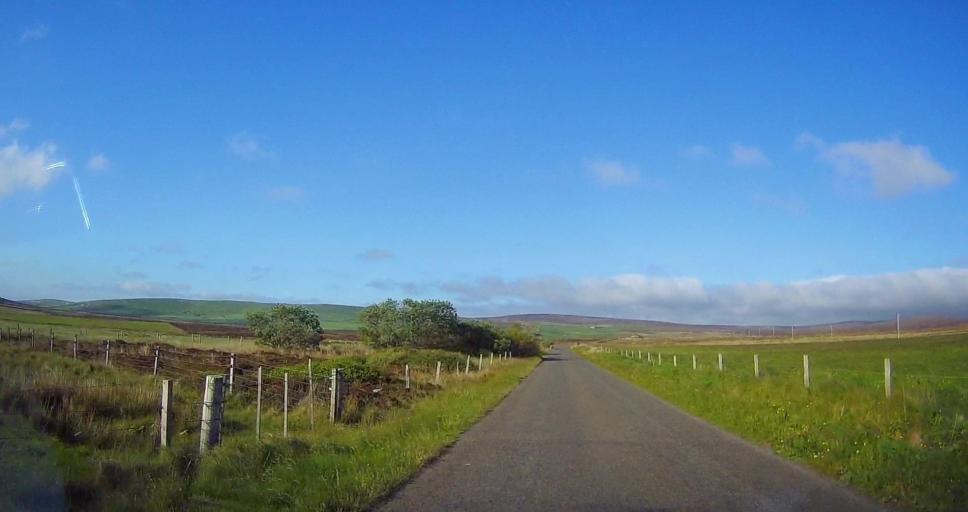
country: GB
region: Scotland
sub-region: Orkney Islands
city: Stromness
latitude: 59.0769
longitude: -3.2026
